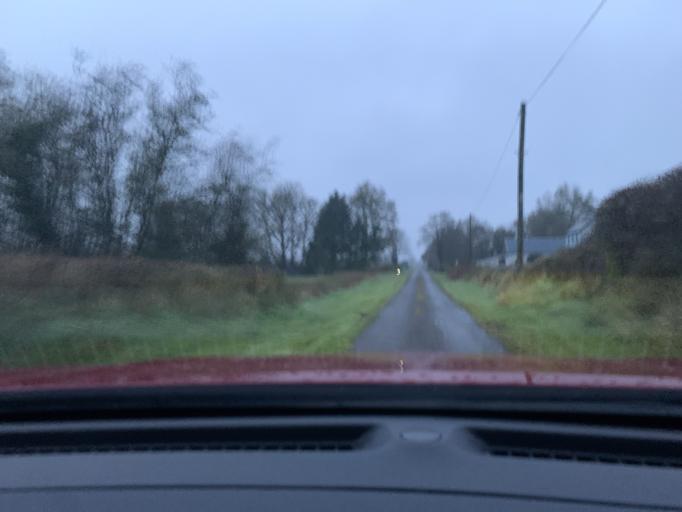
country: IE
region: Connaught
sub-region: Sligo
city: Ballymote
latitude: 54.0195
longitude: -8.5454
